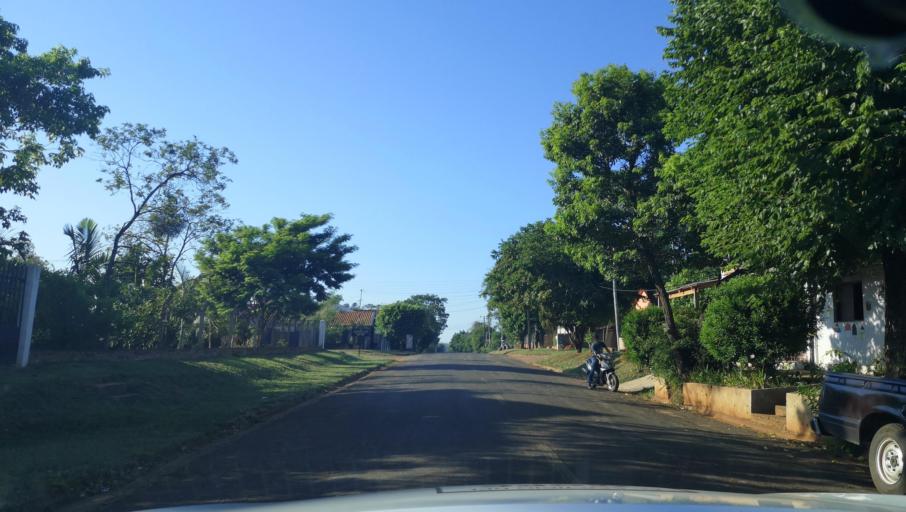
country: PY
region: Itapua
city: Carmen del Parana
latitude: -27.1569
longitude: -56.2450
